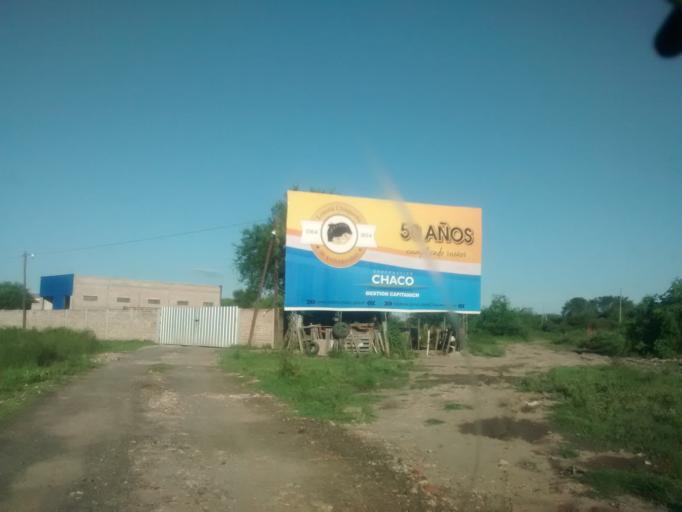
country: AR
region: Chaco
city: Fontana
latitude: -27.4733
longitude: -59.0532
